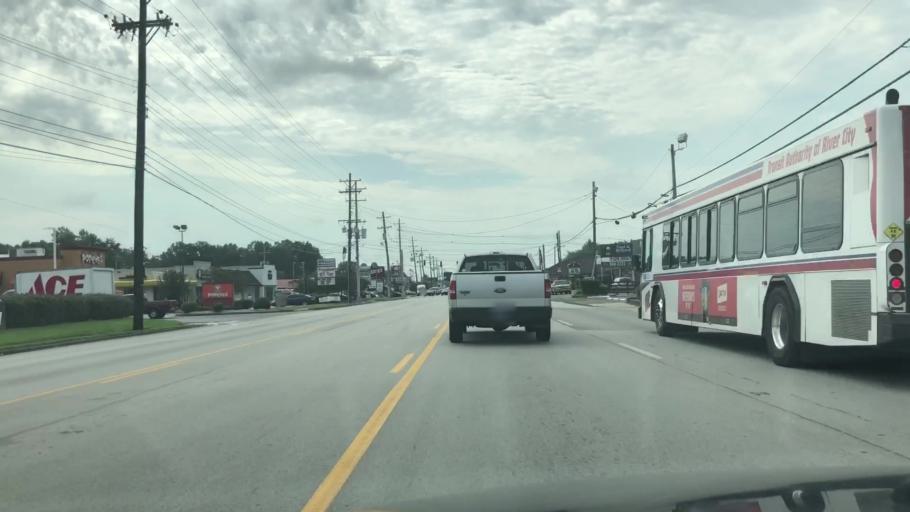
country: US
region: Kentucky
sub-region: Jefferson County
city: Audubon Park
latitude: 38.1758
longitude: -85.7141
